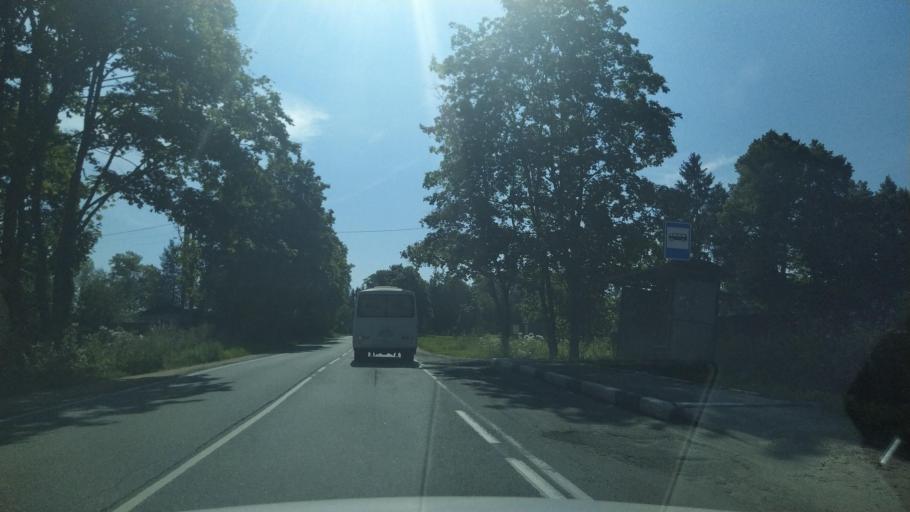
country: RU
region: Leningrad
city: Siverskiy
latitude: 59.3180
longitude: 30.0702
